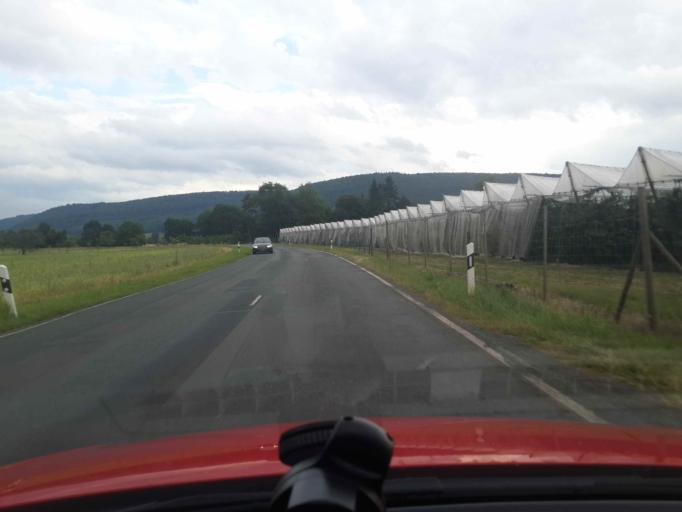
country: DE
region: Bavaria
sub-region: Regierungsbezirk Unterfranken
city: Laudenbach
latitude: 49.7535
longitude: 9.1797
